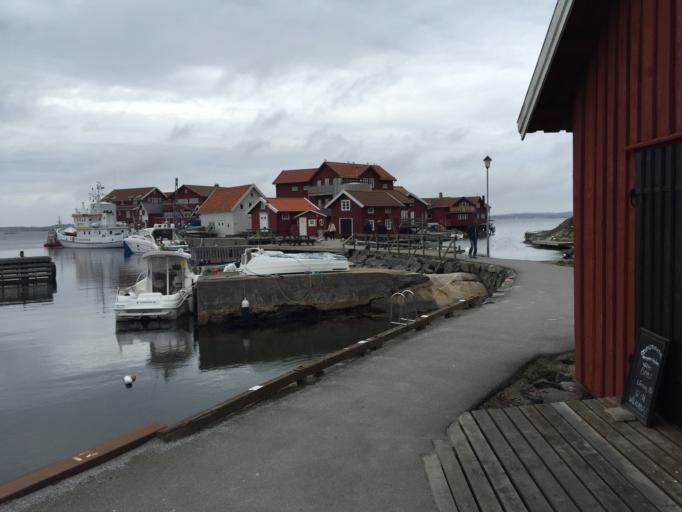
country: SE
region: Vaestra Goetaland
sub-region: Lysekils Kommun
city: Lysekil
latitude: 58.1118
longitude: 11.3666
